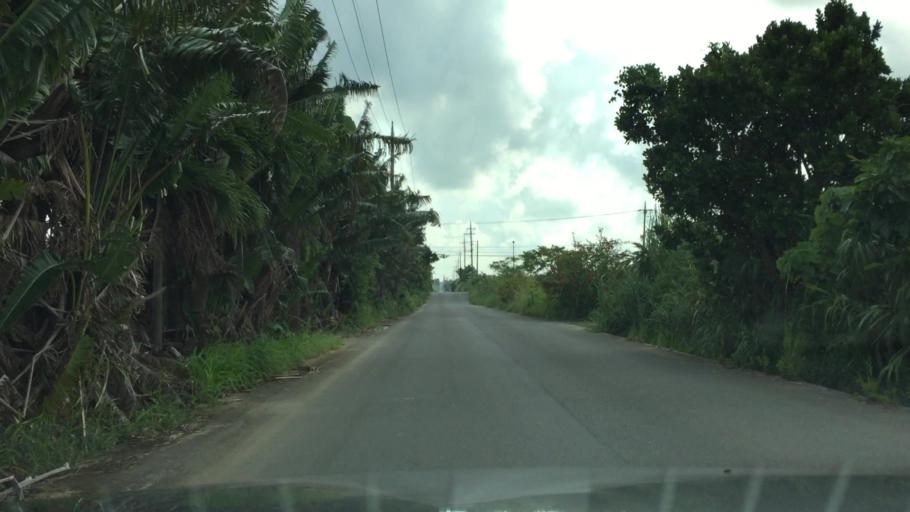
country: JP
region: Okinawa
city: Ishigaki
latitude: 24.3980
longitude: 124.1963
